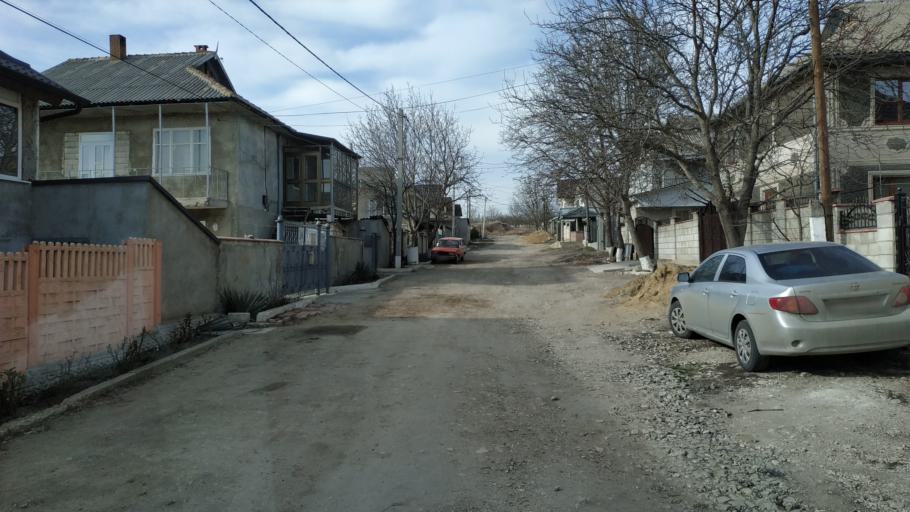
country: MD
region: Chisinau
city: Vatra
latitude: 47.0795
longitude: 28.6892
